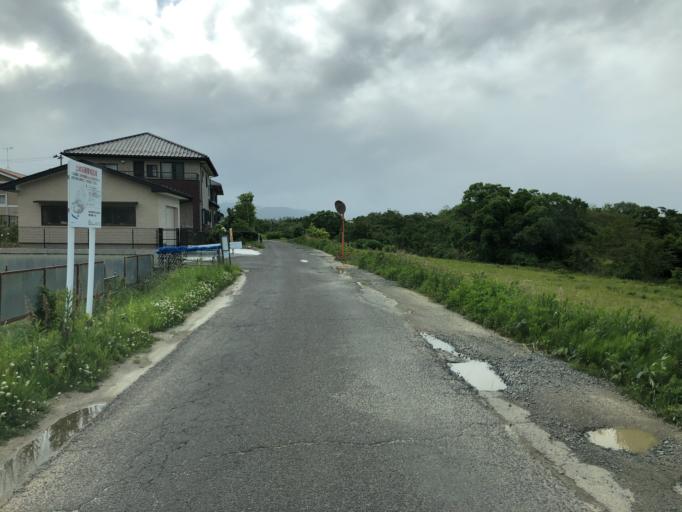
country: JP
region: Fukushima
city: Fukushima-shi
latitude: 37.7807
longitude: 140.4802
